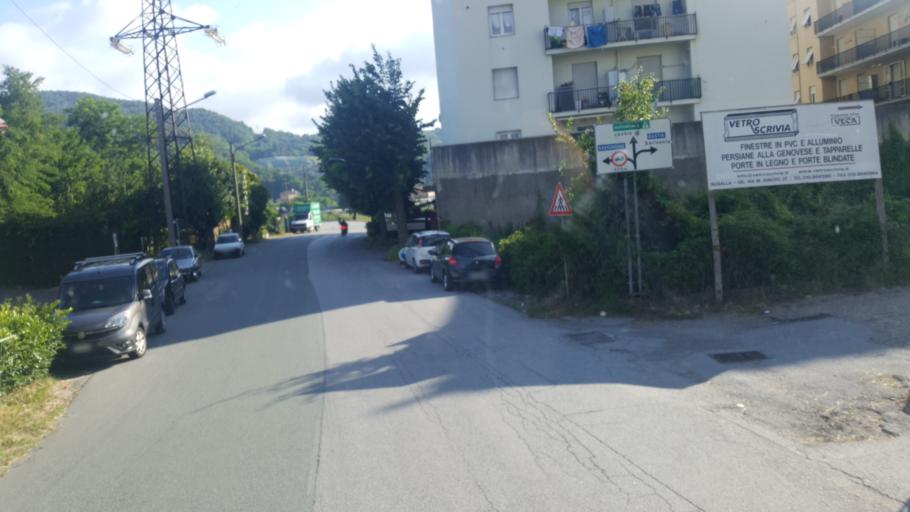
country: IT
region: Liguria
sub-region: Provincia di Genova
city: Busalla
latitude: 44.5732
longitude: 8.9599
